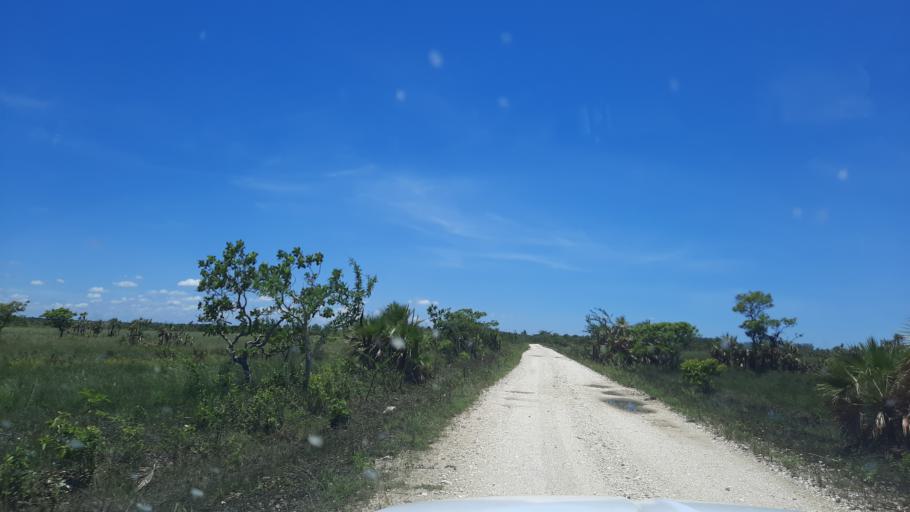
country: BZ
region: Cayo
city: Belmopan
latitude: 17.3916
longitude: -88.4901
